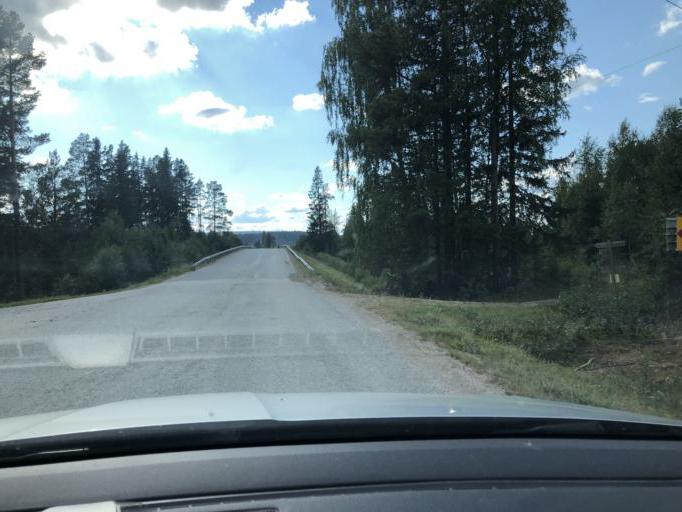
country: SE
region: Vaesternorrland
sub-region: Solleftea Kommun
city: Solleftea
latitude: 63.3152
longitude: 17.2144
